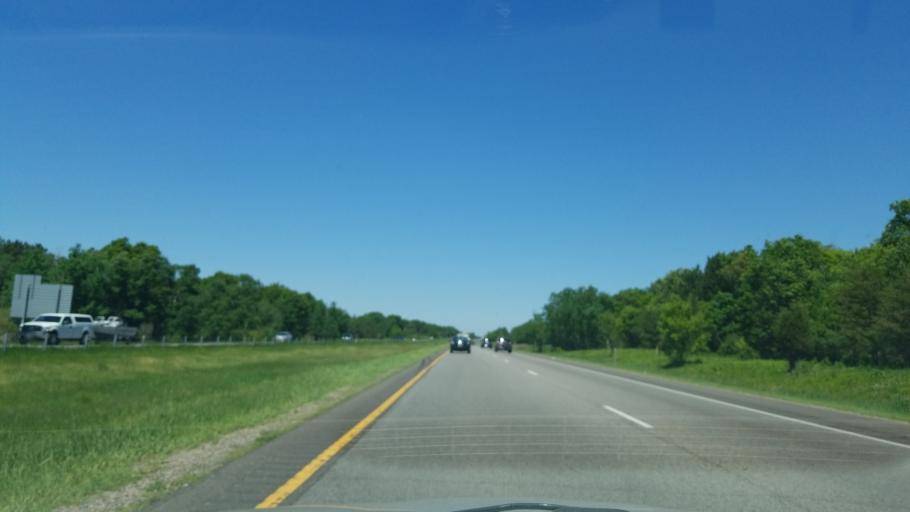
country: US
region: Minnesota
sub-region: Chisago County
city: Wyoming
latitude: 45.3057
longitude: -93.0028
